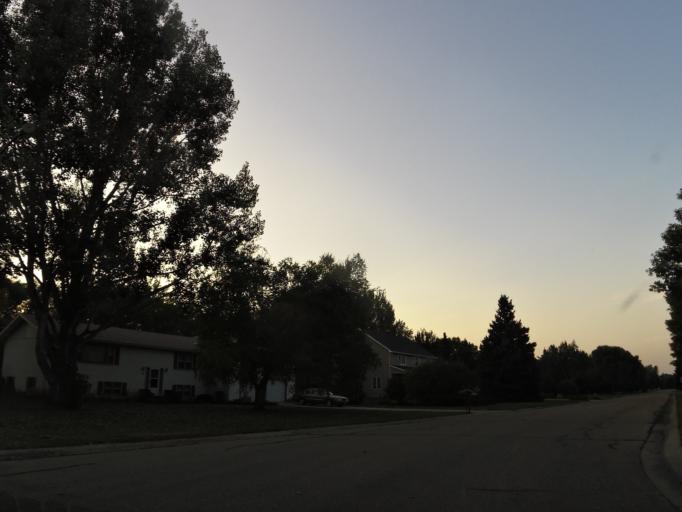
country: US
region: North Dakota
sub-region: Grand Forks County
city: Grand Forks
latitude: 47.8537
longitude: -97.0115
